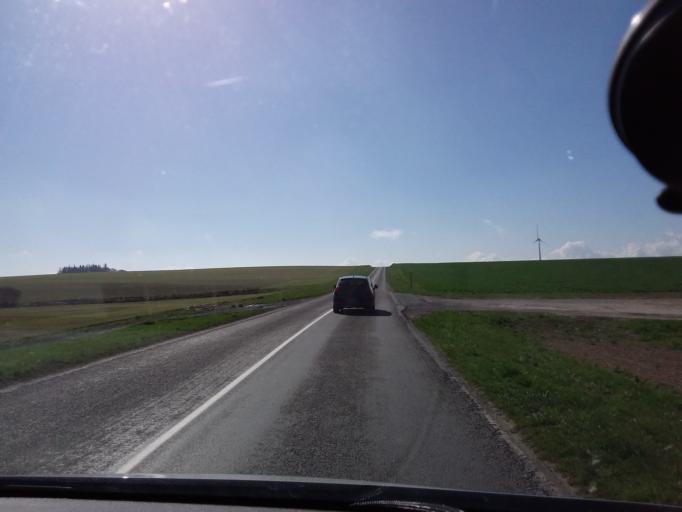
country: FR
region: Picardie
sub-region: Departement de l'Aisne
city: Guignicourt
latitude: 49.5246
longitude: 4.0439
